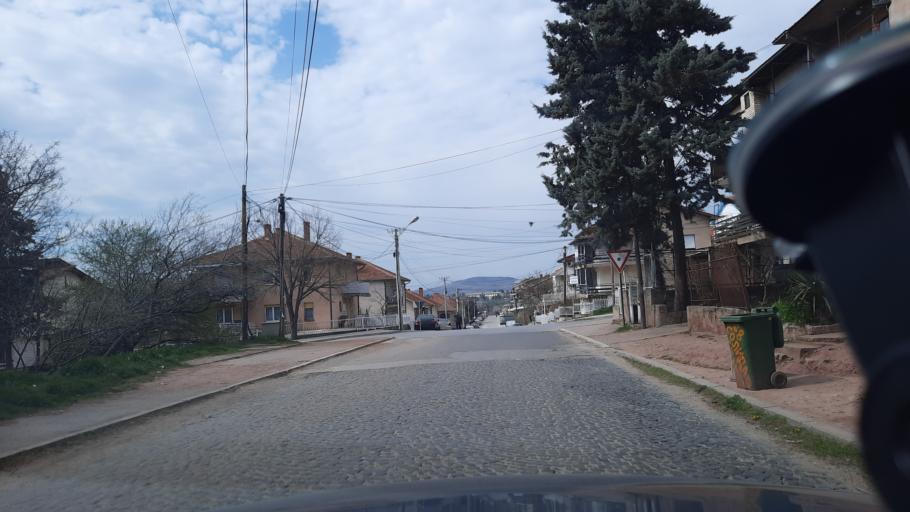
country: MK
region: Stip
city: Shtip
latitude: 41.7465
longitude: 22.1974
